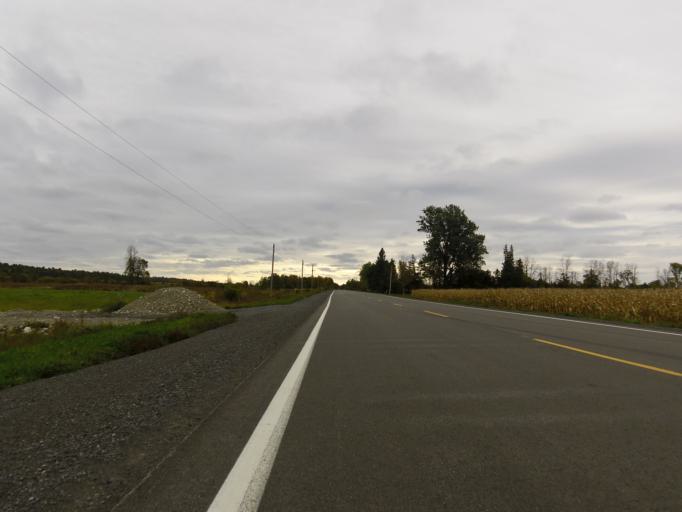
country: CA
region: Ontario
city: Arnprior
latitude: 45.4868
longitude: -76.1880
